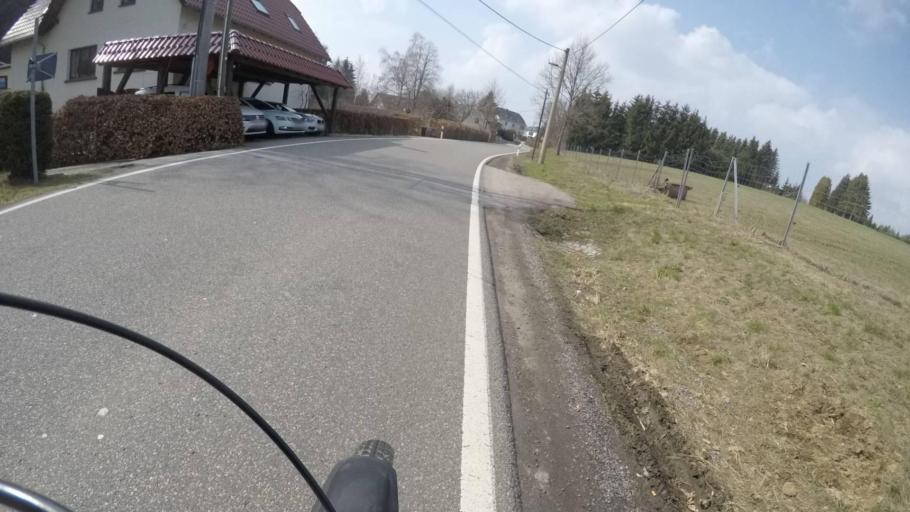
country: DE
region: Saxony
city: Limbach-Oberfrohna
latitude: 50.8296
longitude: 12.7419
